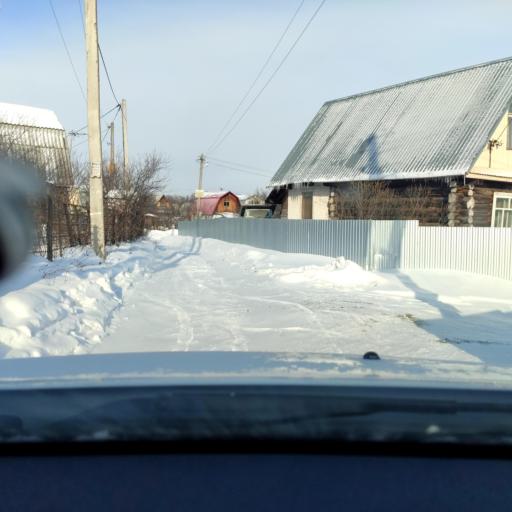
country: RU
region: Bashkortostan
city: Avdon
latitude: 54.7178
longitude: 55.7812
